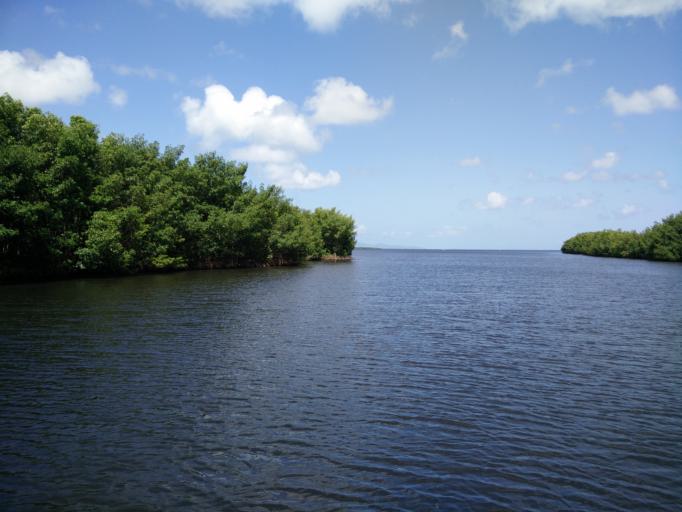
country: GP
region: Guadeloupe
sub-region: Guadeloupe
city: Petit-Canal
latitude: 16.3538
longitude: -61.4933
